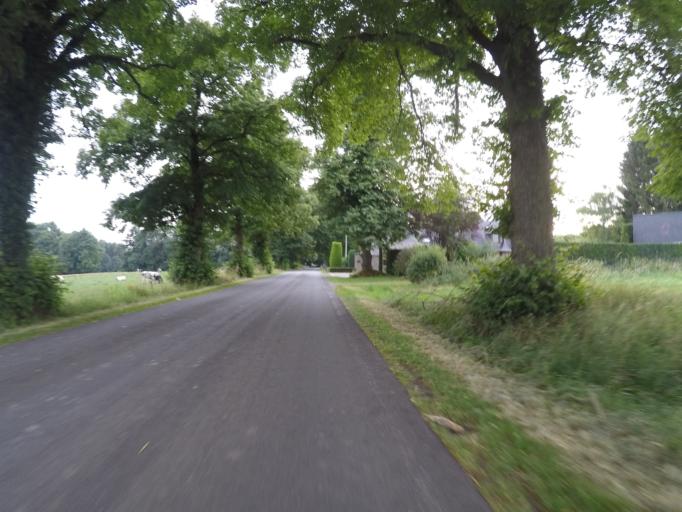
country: BE
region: Wallonia
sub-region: Province de Namur
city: Assesse
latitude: 50.3451
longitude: 5.0309
